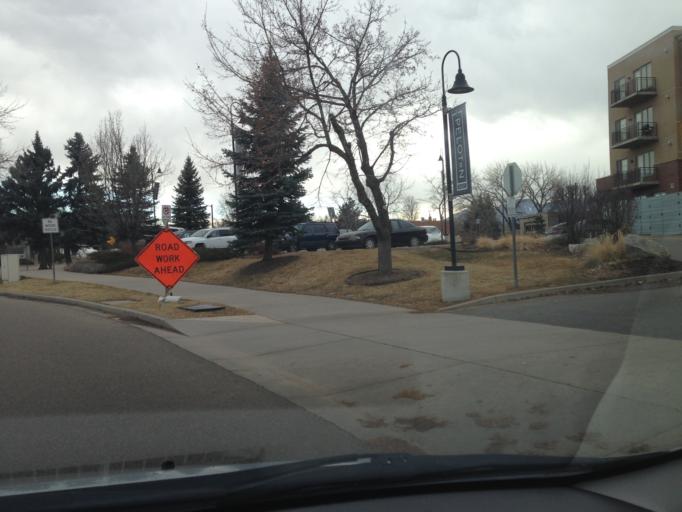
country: US
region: Colorado
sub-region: Boulder County
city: Boulder
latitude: 40.0158
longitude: -105.2470
